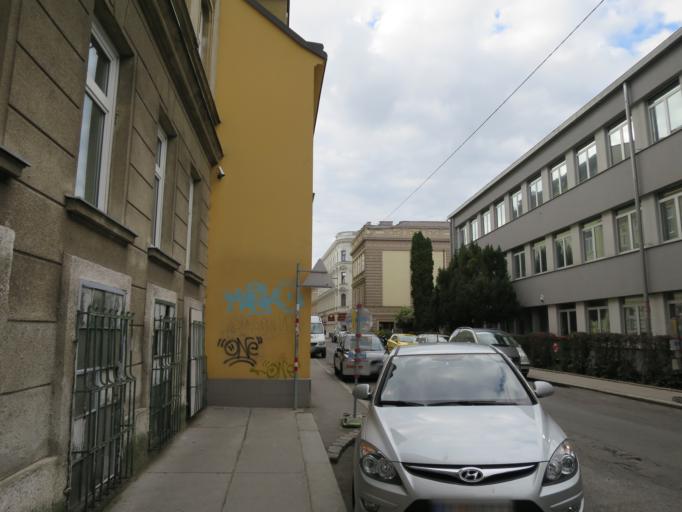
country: AT
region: Vienna
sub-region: Wien Stadt
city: Vienna
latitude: 48.2164
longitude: 16.3331
